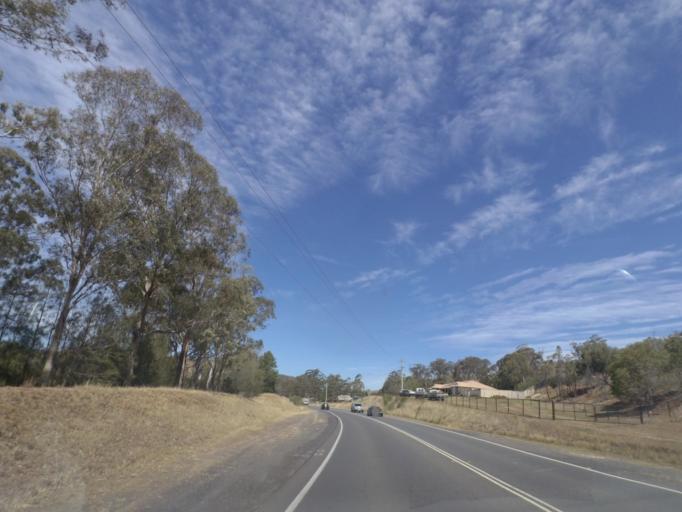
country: AU
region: New South Wales
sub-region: Wollondilly
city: Picton
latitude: -34.1664
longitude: 150.6233
